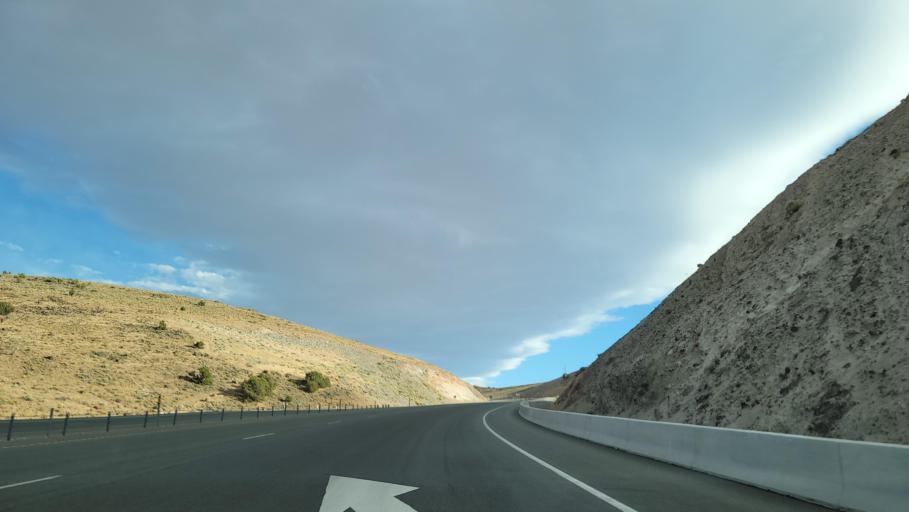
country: US
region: Nevada
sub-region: Lyon County
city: Stagecoach
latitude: 39.4870
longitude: -119.4012
